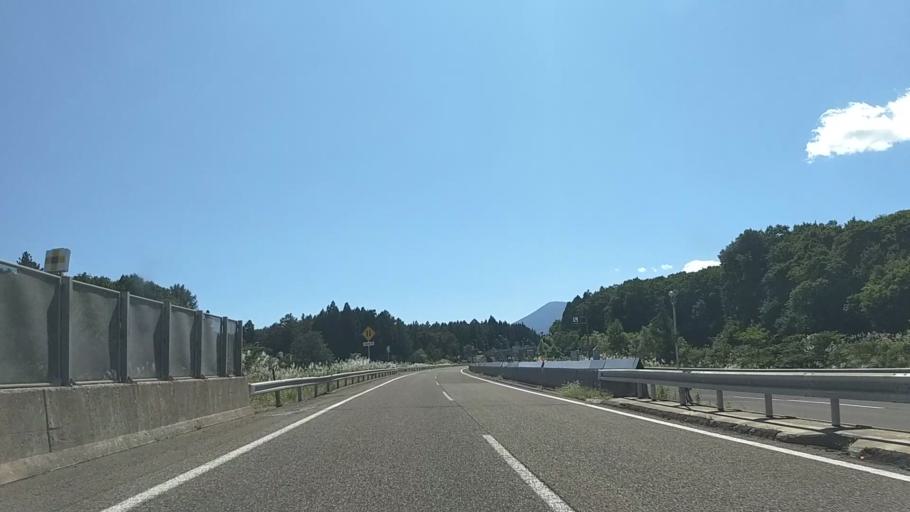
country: JP
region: Niigata
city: Arai
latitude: 36.8657
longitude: 138.1944
